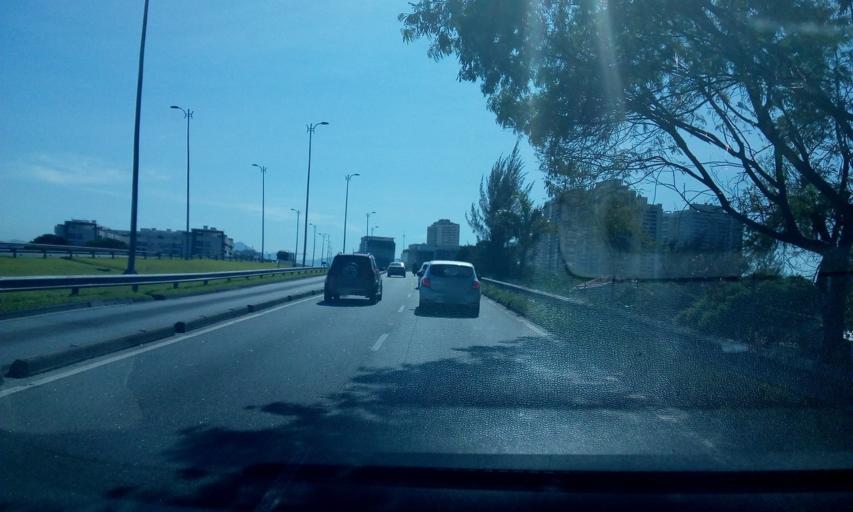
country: BR
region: Rio de Janeiro
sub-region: Nilopolis
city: Nilopolis
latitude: -23.0212
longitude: -43.4953
